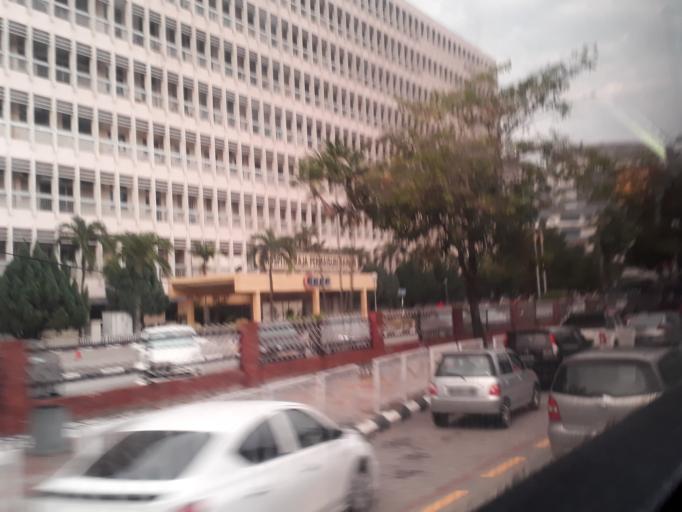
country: MY
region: Perak
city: Ipoh
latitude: 4.6044
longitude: 101.0913
